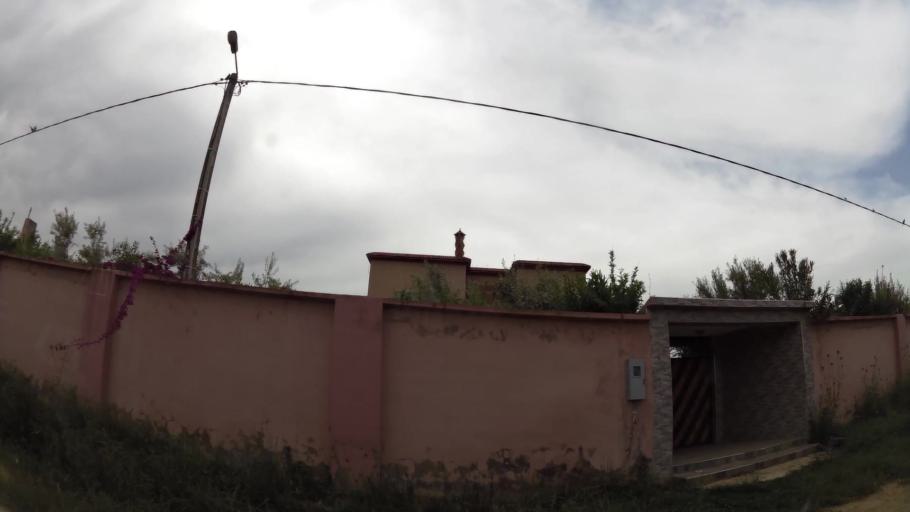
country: MA
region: Rabat-Sale-Zemmour-Zaer
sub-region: Khemisset
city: Khemisset
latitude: 33.7502
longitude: -6.2015
